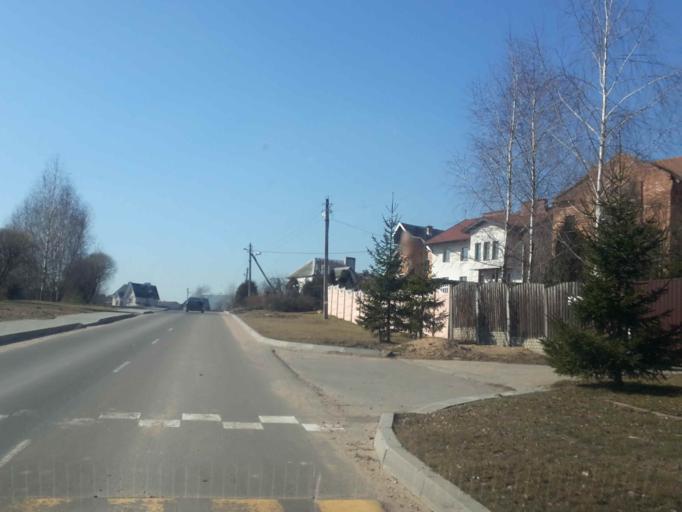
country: BY
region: Minsk
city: Zhdanovichy
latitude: 53.9195
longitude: 27.3999
